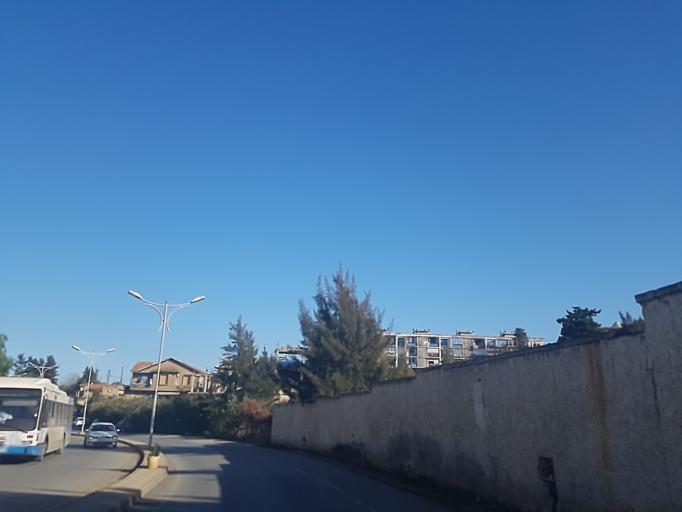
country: DZ
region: Alger
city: Birkhadem
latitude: 36.7330
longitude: 3.1031
